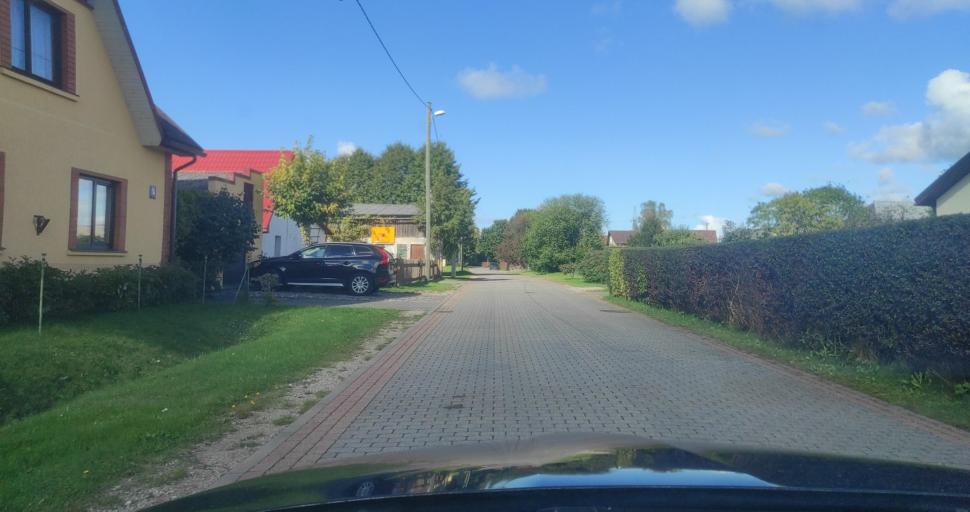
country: LV
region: Ventspils
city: Ventspils
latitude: 57.3838
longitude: 21.6106
